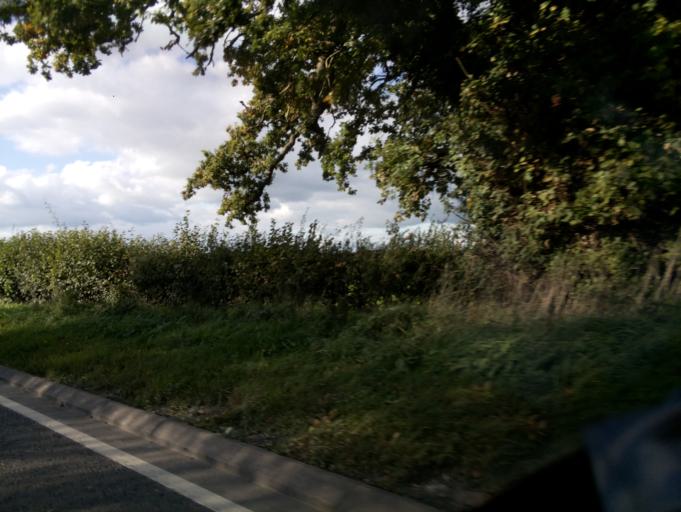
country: GB
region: England
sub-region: Herefordshire
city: Kinnersley
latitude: 52.1200
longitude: -2.9913
